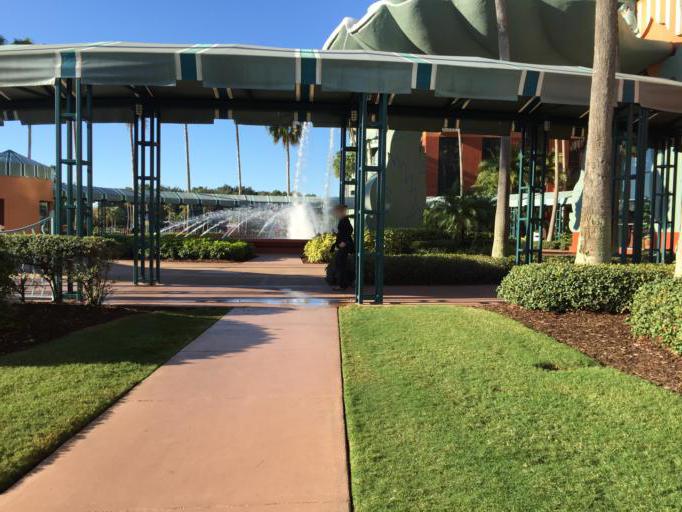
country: US
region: Florida
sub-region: Osceola County
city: Celebration
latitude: 28.3671
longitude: -81.5598
